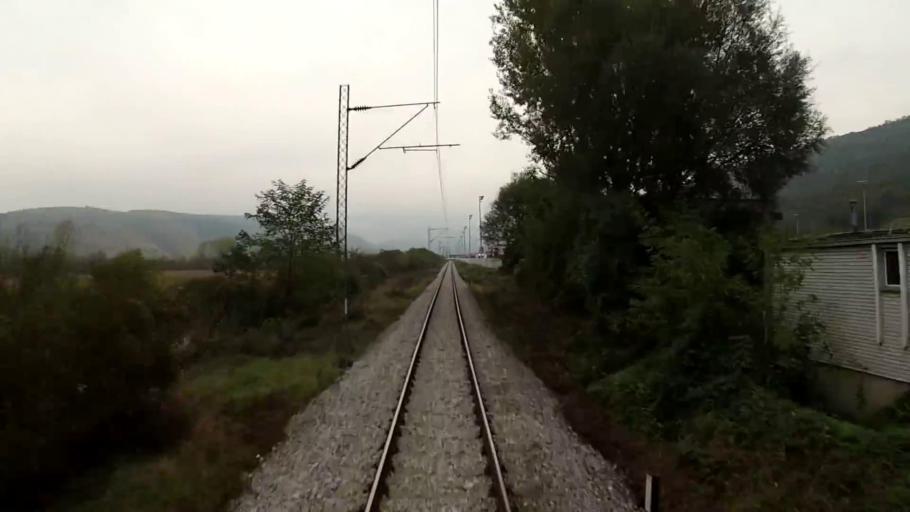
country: RS
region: Central Serbia
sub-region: Pirotski Okrug
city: Dimitrovgrad
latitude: 43.0022
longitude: 22.8219
